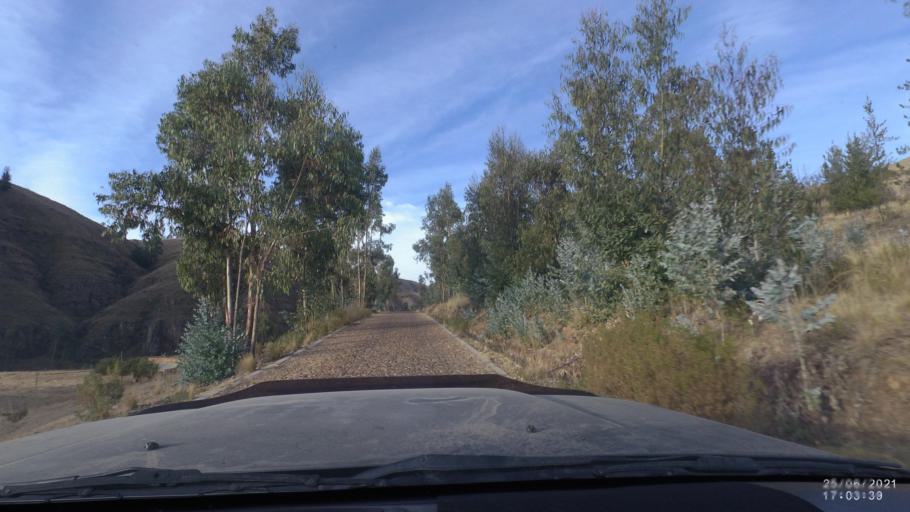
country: BO
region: Cochabamba
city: Arani
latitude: -17.8344
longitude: -65.7274
